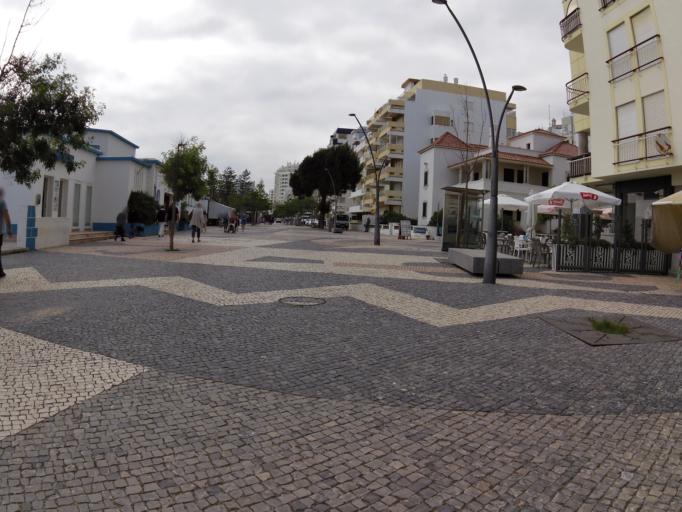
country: PT
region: Faro
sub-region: Silves
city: Armacao de Pera
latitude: 37.1016
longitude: -8.3631
